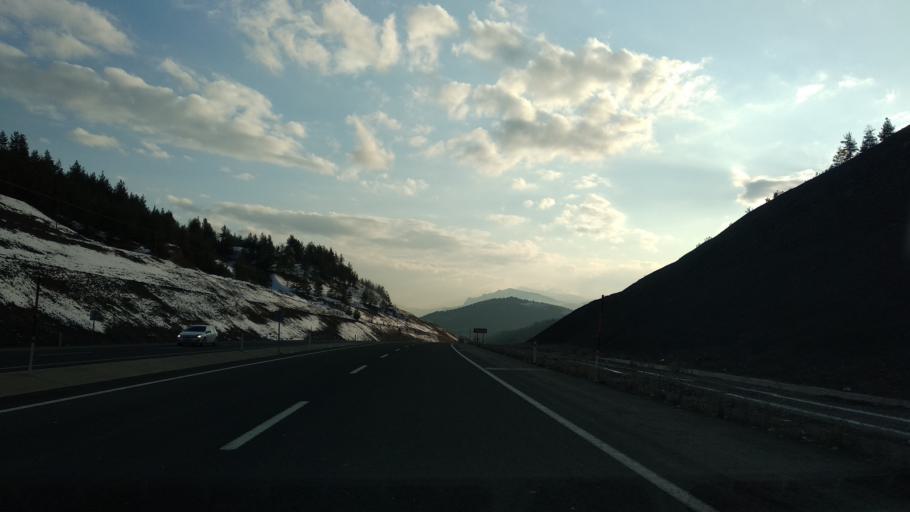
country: TR
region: Kahramanmaras
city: Yenicekale
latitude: 37.7156
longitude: 36.6953
